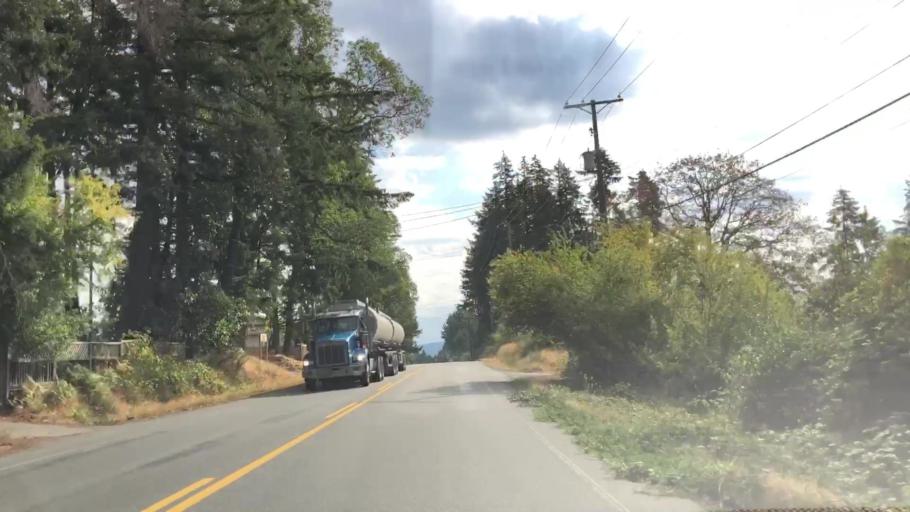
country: CA
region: British Columbia
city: North Saanich
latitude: 48.6866
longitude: -123.5574
